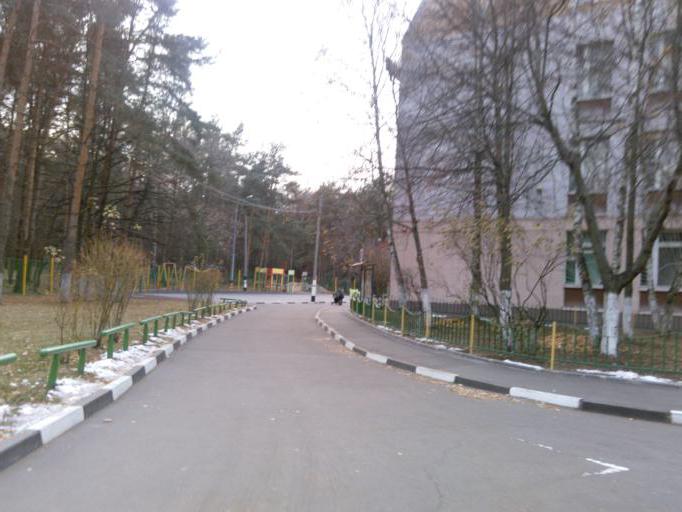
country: RU
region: Moscow
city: Troparevo
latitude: 55.6572
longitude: 37.5132
